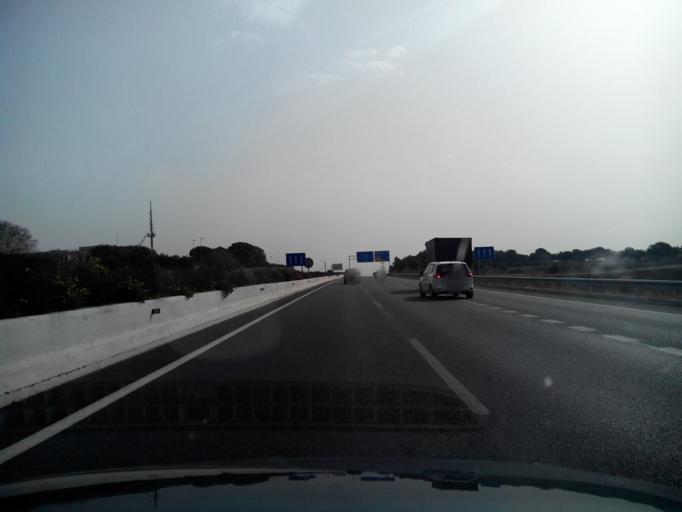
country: ES
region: Catalonia
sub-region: Provincia de Tarragona
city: Constanti
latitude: 41.1327
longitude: 1.1853
